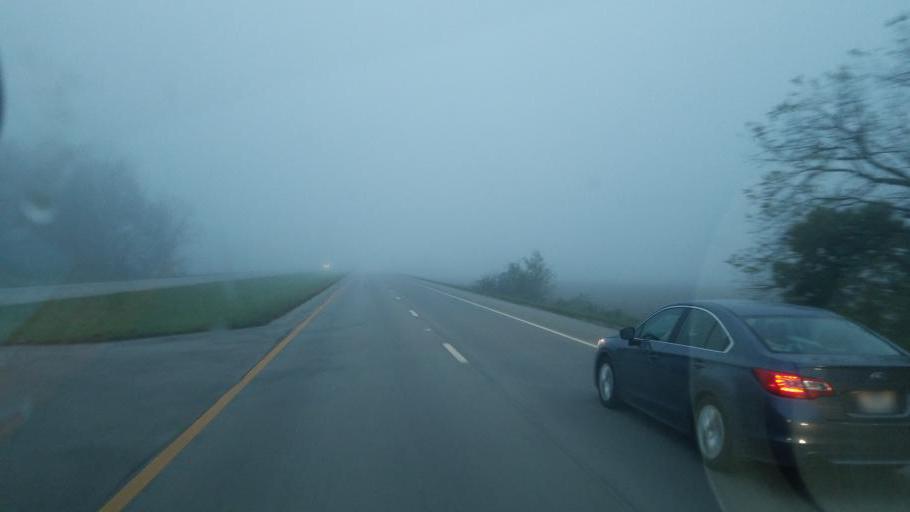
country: US
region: Ohio
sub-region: Pike County
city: Piketon
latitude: 38.9879
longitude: -83.0234
